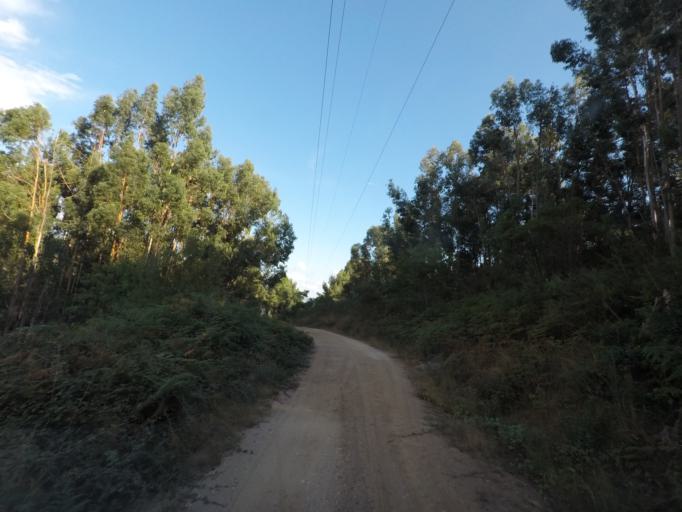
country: PT
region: Vila Real
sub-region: Mesao Frio
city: Mesao Frio
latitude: 41.1710
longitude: -7.9060
